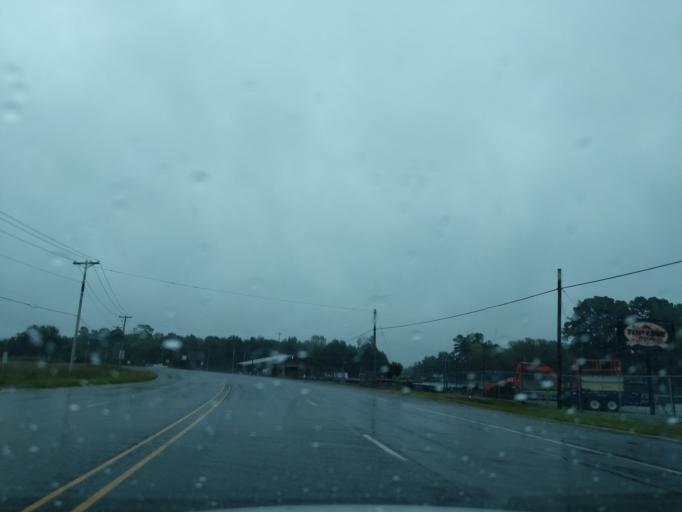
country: US
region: Texas
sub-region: Panola County
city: Carthage
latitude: 32.1573
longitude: -94.3264
